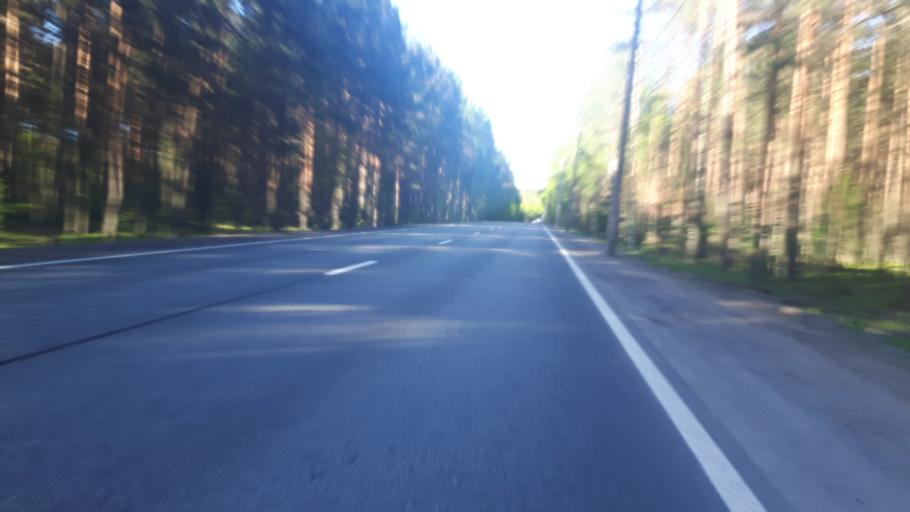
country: RU
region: Leningrad
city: Molodezhnoye
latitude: 60.1774
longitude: 29.4454
